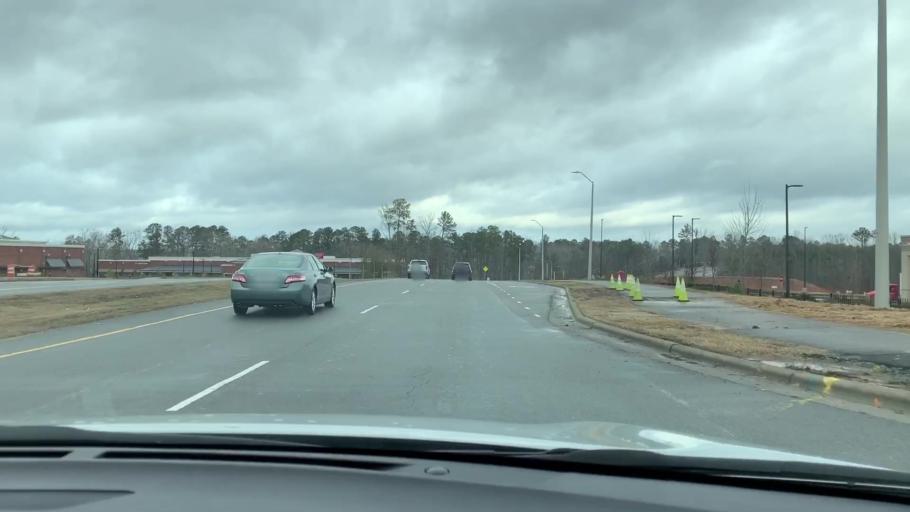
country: US
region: North Carolina
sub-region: Wake County
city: Green Level
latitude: 35.8227
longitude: -78.9021
